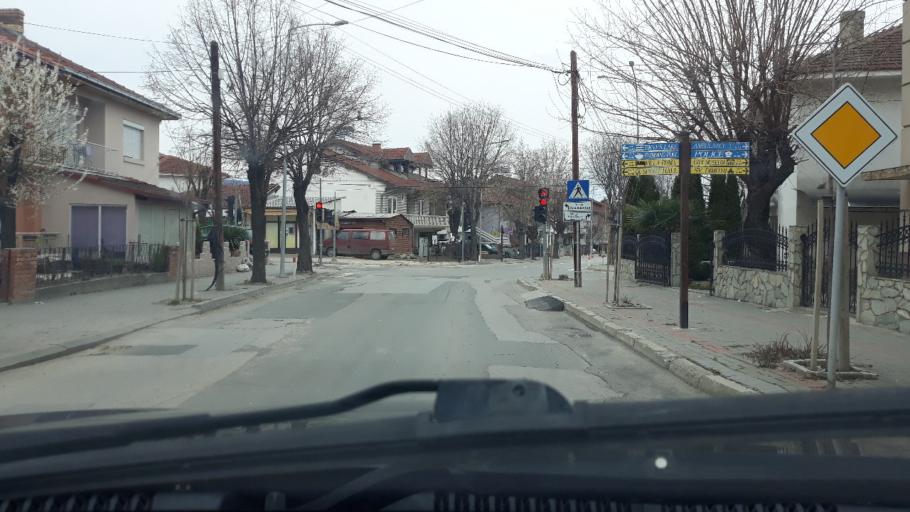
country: MK
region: Kavadarci
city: Kavadarci
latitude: 41.4332
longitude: 22.0076
